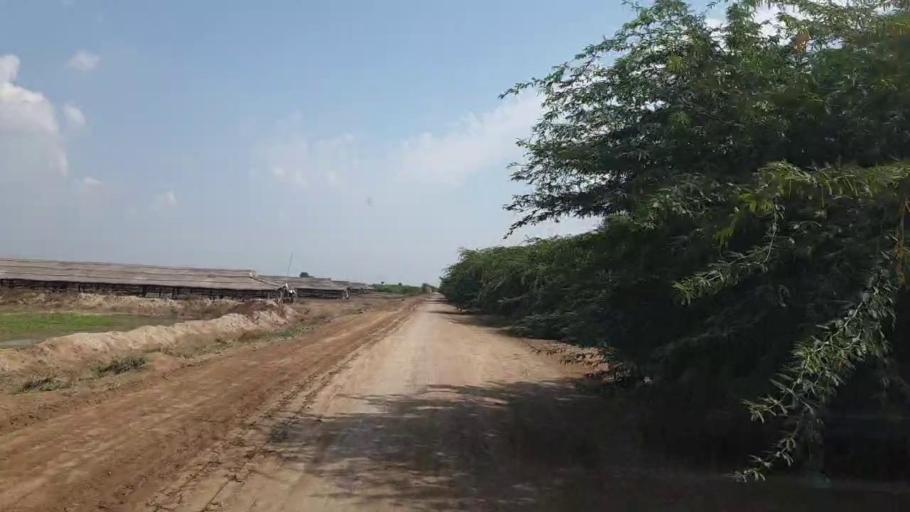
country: PK
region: Sindh
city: Badin
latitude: 24.4774
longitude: 68.6313
